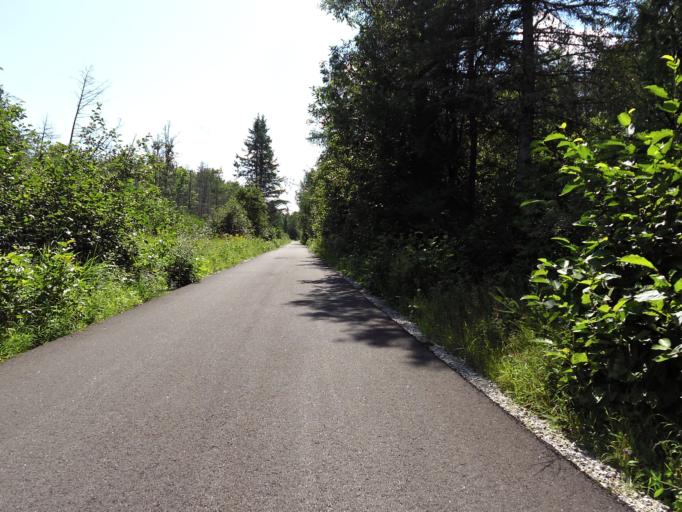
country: CA
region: Quebec
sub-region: Outaouais
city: Maniwaki
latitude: 46.1746
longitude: -76.0409
